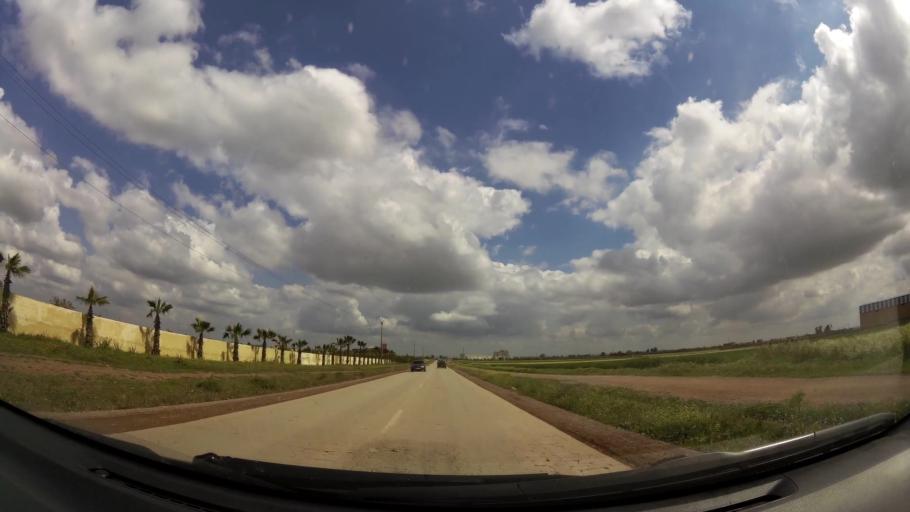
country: MA
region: Chaouia-Ouardigha
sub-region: Settat Province
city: Berrechid
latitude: 33.2739
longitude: -7.6402
